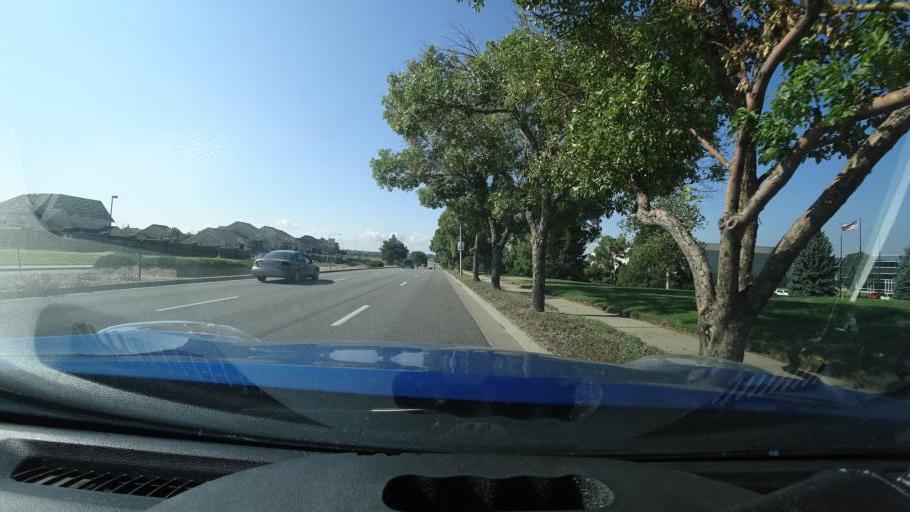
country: US
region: Colorado
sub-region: Adams County
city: Aurora
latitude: 39.7161
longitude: -104.7913
